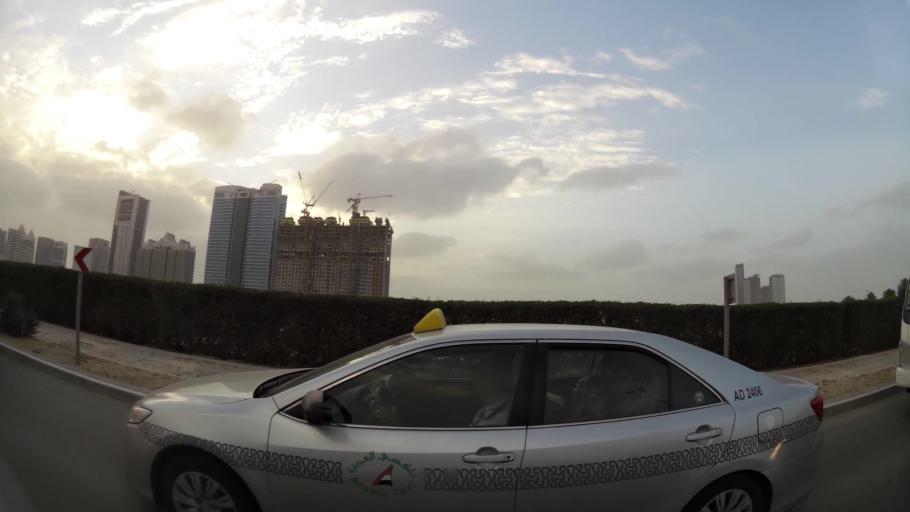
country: AE
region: Abu Dhabi
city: Abu Dhabi
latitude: 24.5078
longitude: 54.3815
